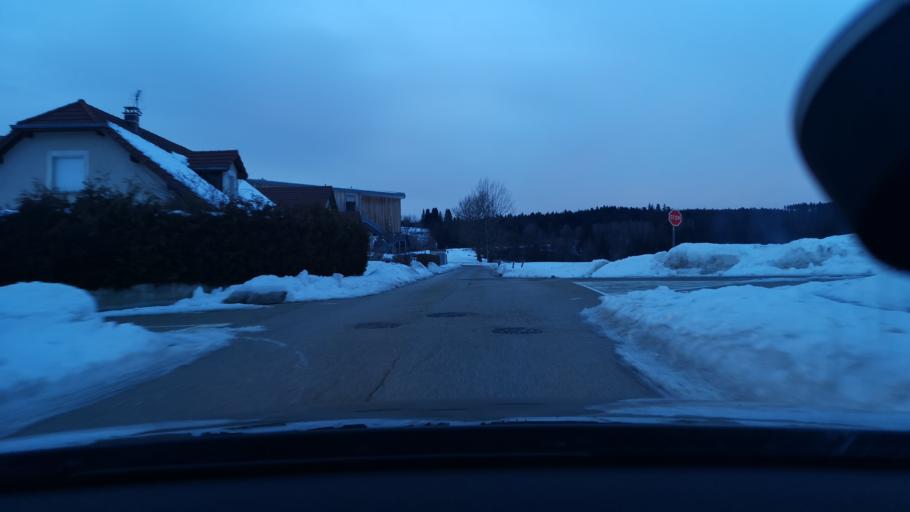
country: FR
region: Franche-Comte
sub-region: Departement du Doubs
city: Pontarlier
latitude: 46.9031
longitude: 6.3716
